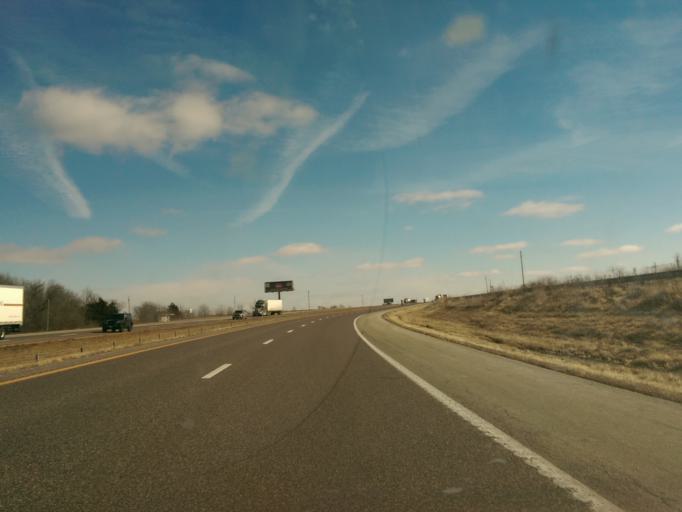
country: US
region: Missouri
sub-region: Callaway County
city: Fulton
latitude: 38.9435
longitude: -91.8815
